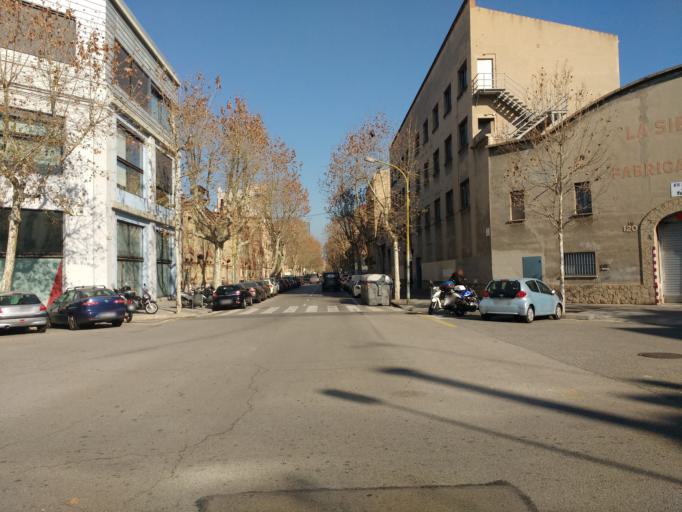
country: ES
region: Catalonia
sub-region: Provincia de Barcelona
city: Sant Marti
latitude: 41.3946
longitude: 2.1983
